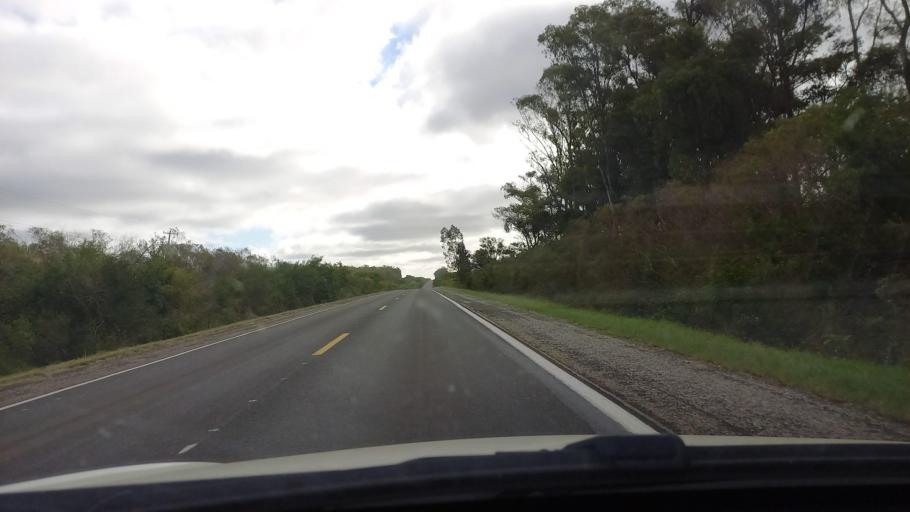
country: BR
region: Rio Grande do Sul
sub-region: Dom Pedrito
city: Dom Pedrito
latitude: -30.9146
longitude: -54.8001
